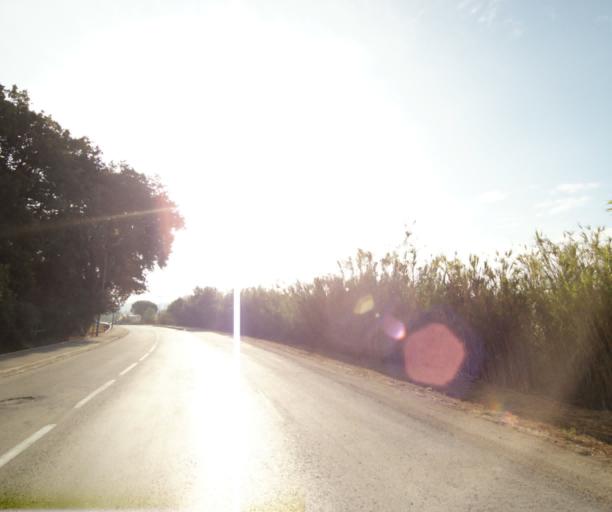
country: FR
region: Provence-Alpes-Cote d'Azur
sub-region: Departement des Bouches-du-Rhone
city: Saint-Victoret
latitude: 43.4164
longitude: 5.2635
